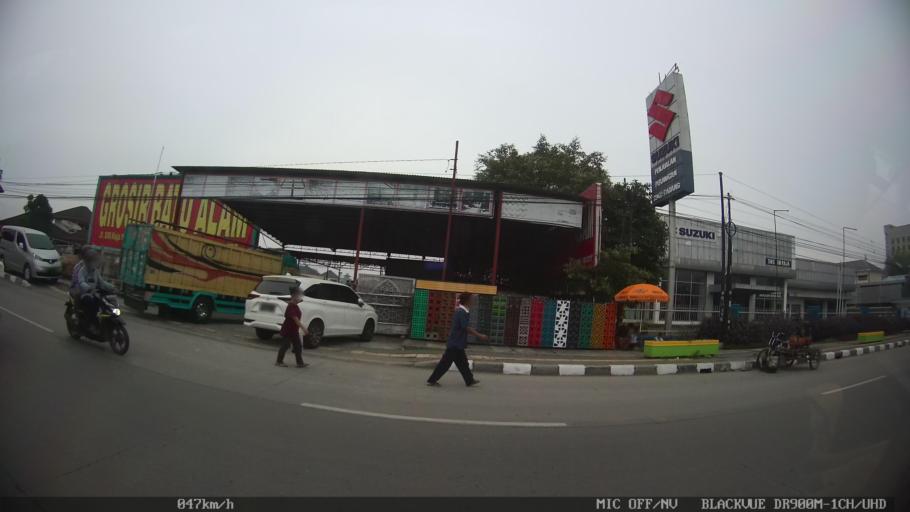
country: ID
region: North Sumatra
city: Deli Tua
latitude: 3.5387
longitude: 98.7033
